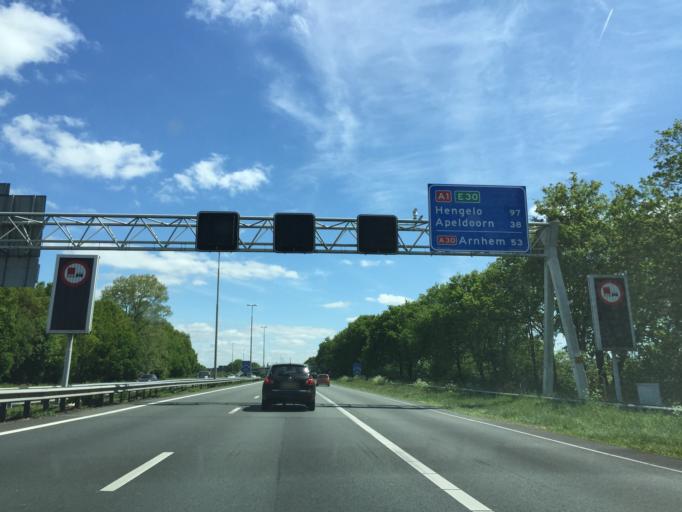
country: NL
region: Utrecht
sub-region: Gemeente Leusden
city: Leusden
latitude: 52.1673
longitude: 5.4498
